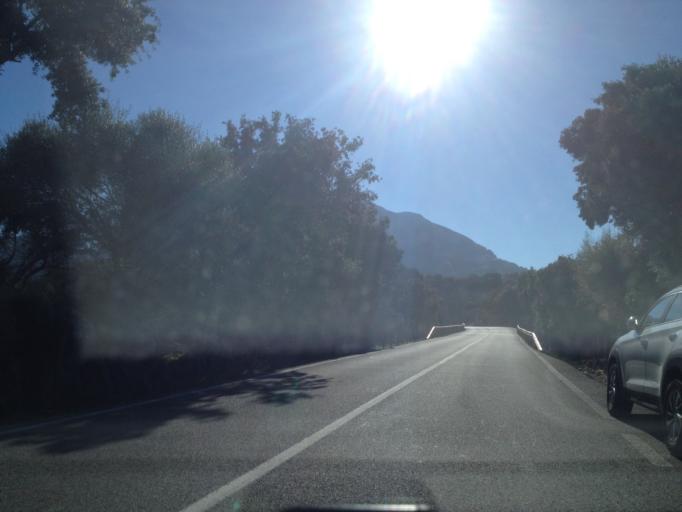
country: ES
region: Balearic Islands
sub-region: Illes Balears
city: Escorca
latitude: 39.8681
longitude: 2.9246
